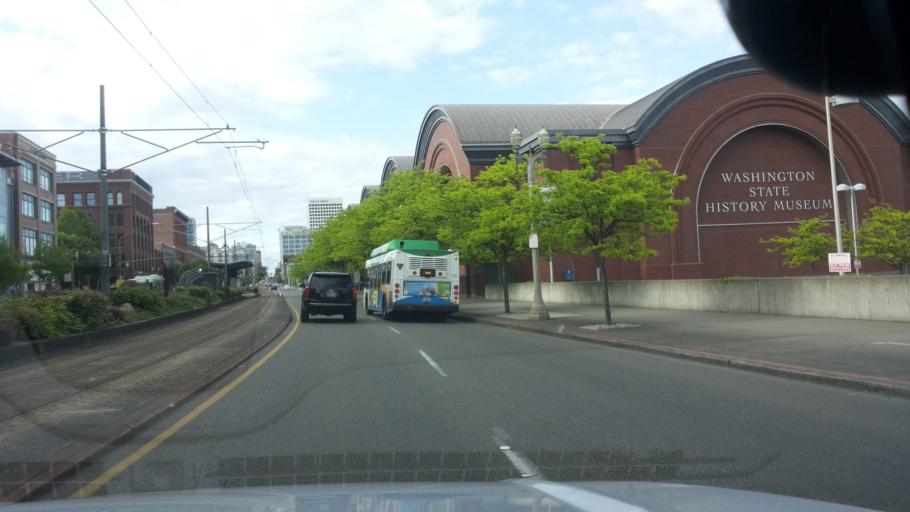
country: US
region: Washington
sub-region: Pierce County
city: Tacoma
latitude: 47.2437
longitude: -122.4363
